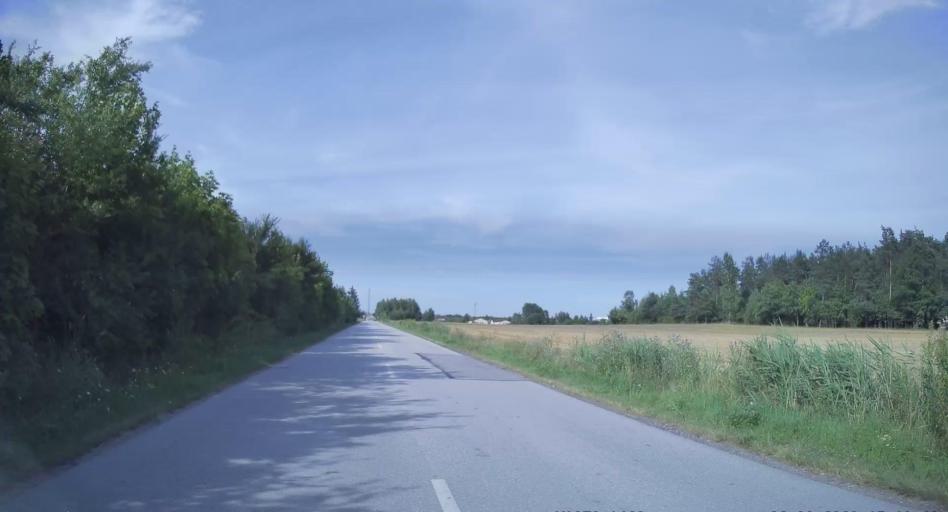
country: PL
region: Lodz Voivodeship
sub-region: Powiat opoczynski
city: Mniszkow
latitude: 51.3651
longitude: 20.0382
